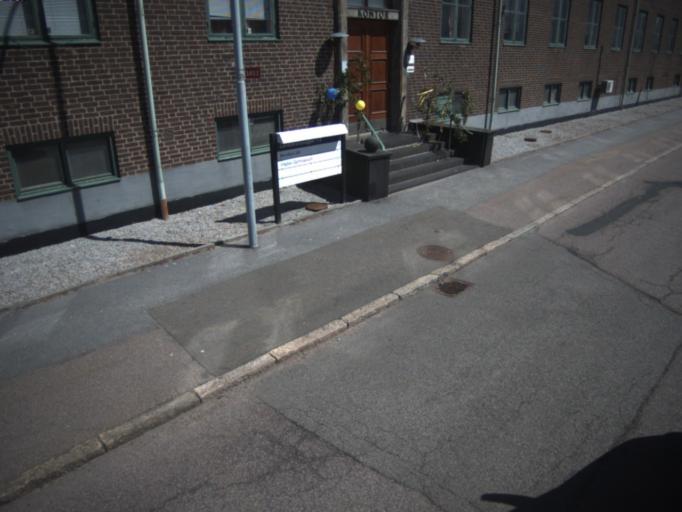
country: SE
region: Skane
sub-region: Helsingborg
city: Helsingborg
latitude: 56.0201
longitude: 12.7275
